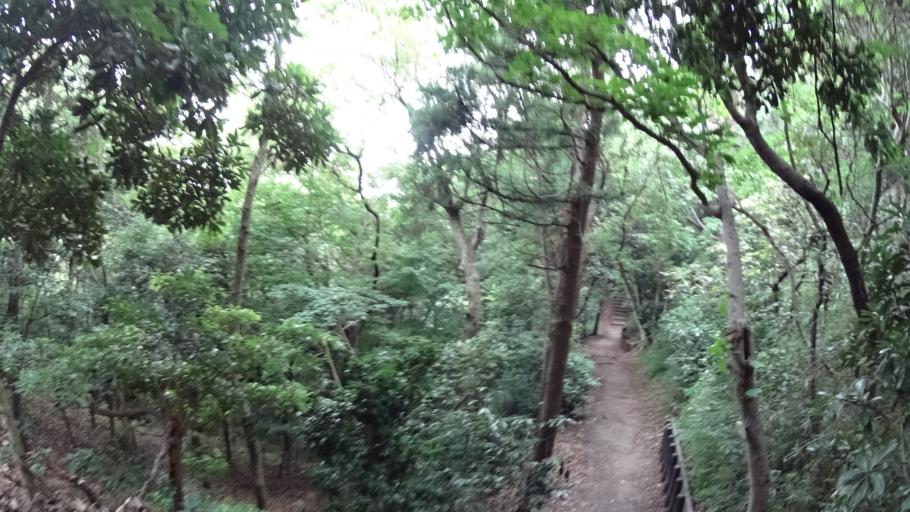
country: JP
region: Kanagawa
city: Zushi
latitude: 35.3565
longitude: 139.6107
